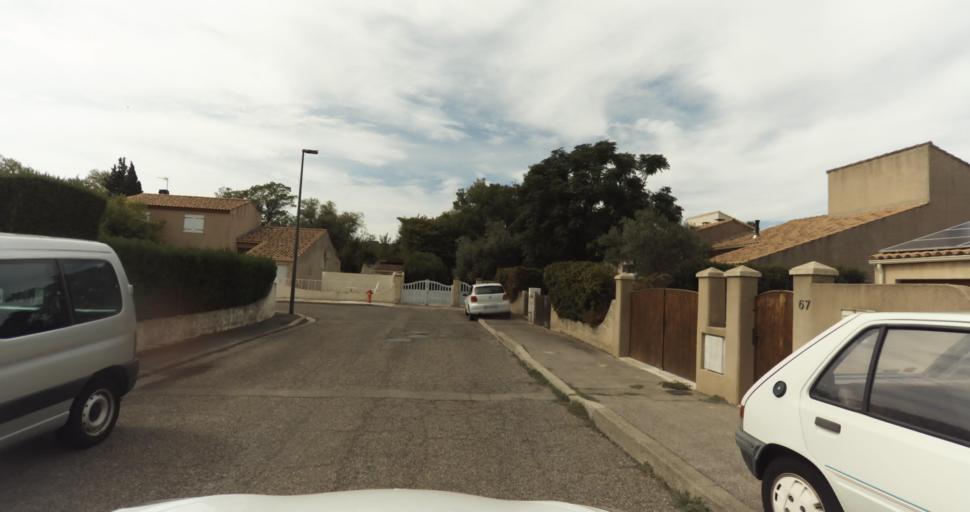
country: FR
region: Provence-Alpes-Cote d'Azur
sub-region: Departement des Bouches-du-Rhone
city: Miramas
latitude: 43.5781
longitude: 4.9930
